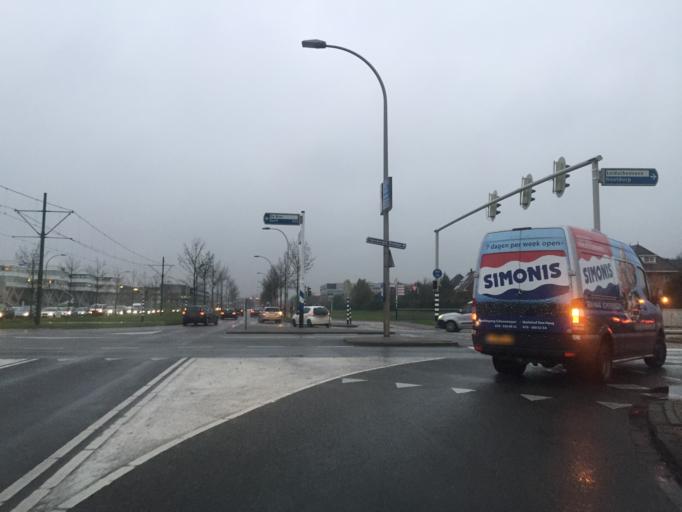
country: NL
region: South Holland
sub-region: Gemeente Den Haag
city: Ypenburg
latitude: 52.0428
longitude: 4.3646
